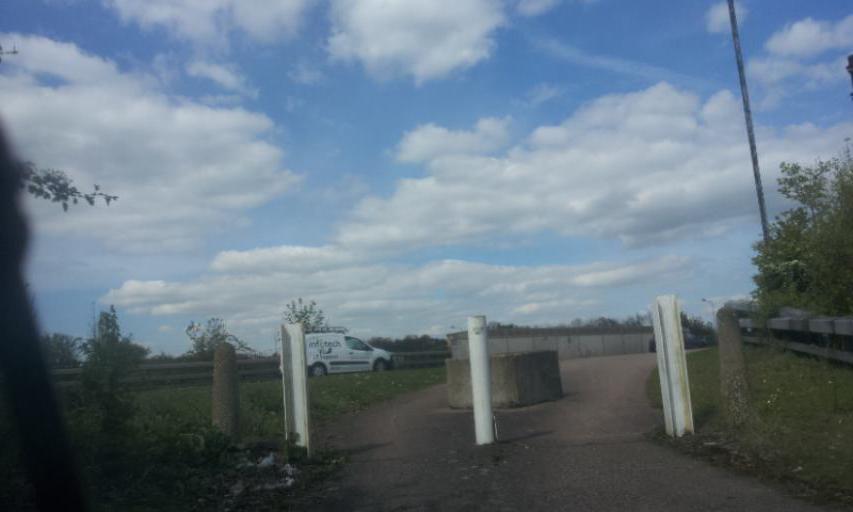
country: GB
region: England
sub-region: Medway
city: Cuxton
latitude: 51.3810
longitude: 0.4689
